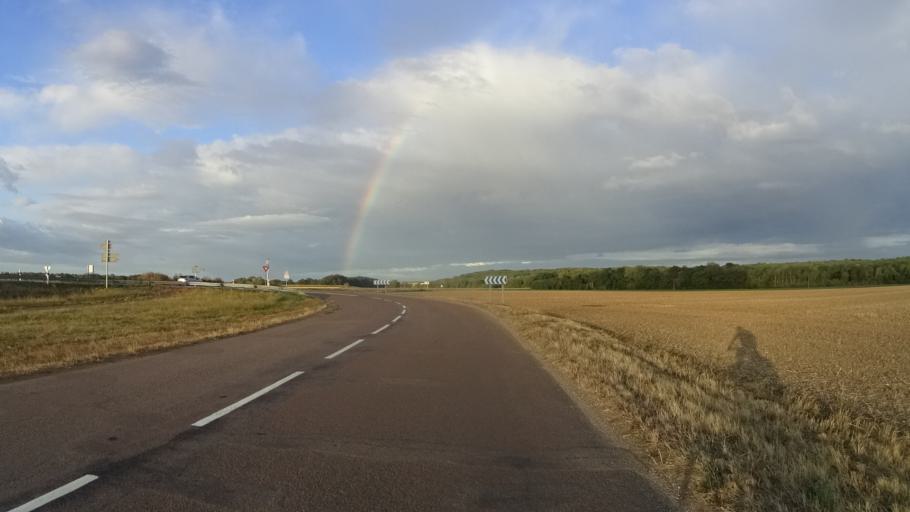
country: FR
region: Bourgogne
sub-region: Departement de la Cote-d'Or
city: Seurre
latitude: 46.9667
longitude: 5.0834
